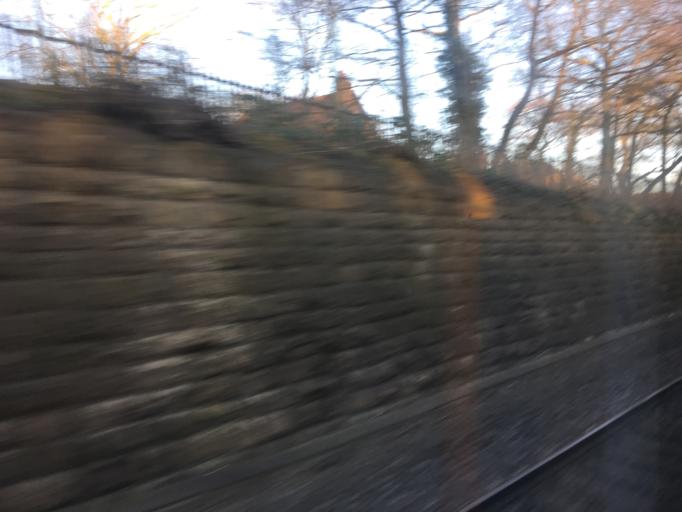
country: GB
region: England
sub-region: Derbyshire
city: Borrowash
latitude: 52.9031
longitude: -1.3822
